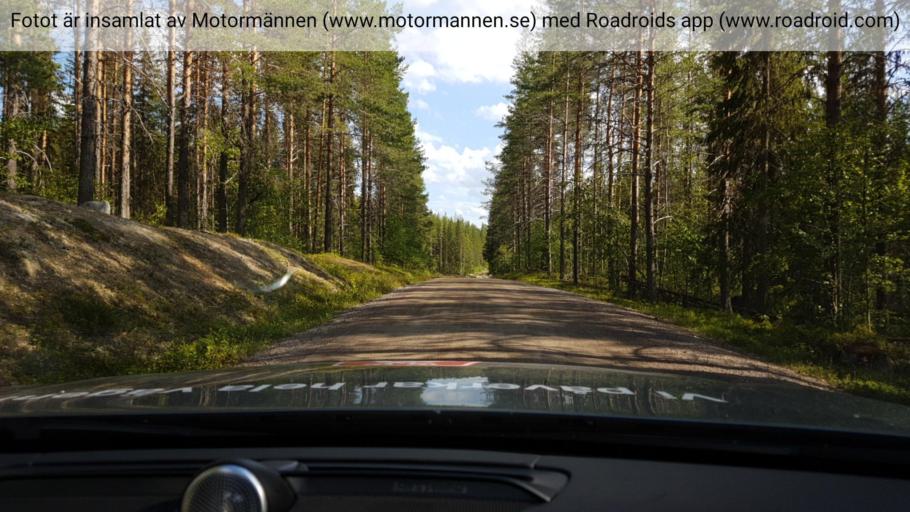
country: SE
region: Vaesterbotten
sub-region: Dorotea Kommun
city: Dorotea
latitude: 63.9679
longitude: 16.0684
